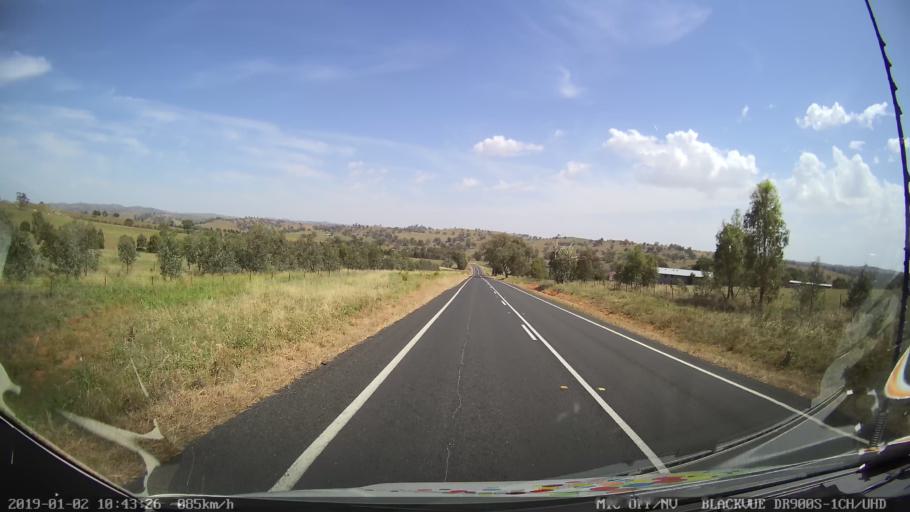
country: AU
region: New South Wales
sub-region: Cootamundra
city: Cootamundra
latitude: -34.7725
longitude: 148.3041
